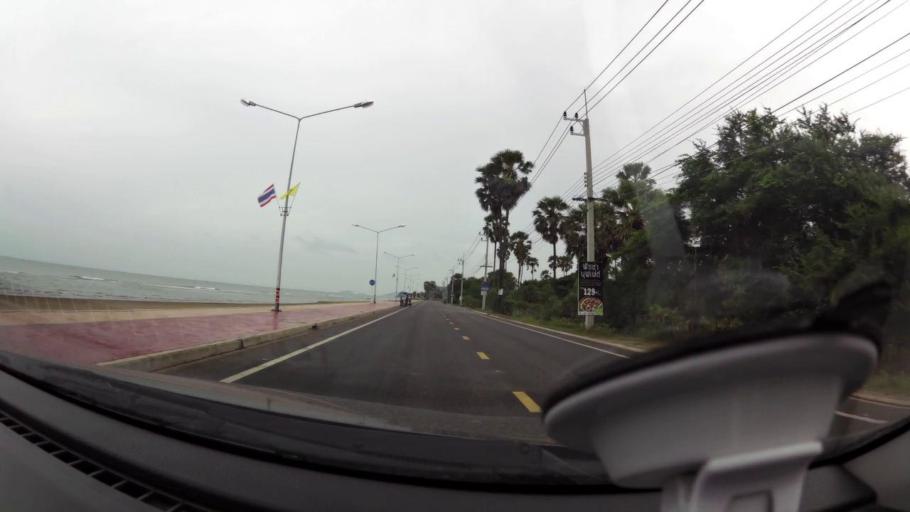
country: TH
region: Prachuap Khiri Khan
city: Pran Buri
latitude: 12.3753
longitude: 100.0002
